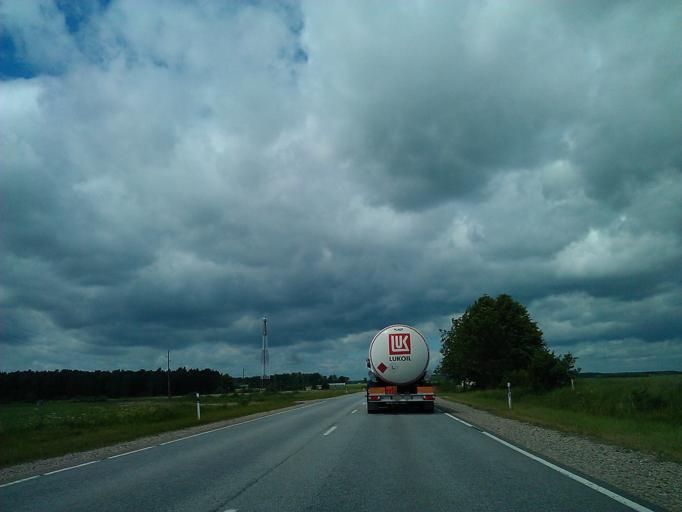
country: LV
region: Engure
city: Smarde
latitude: 56.9154
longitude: 23.3323
